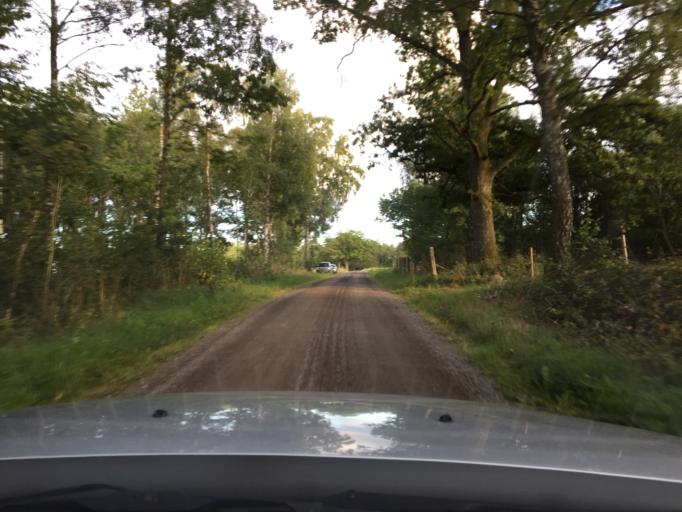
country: SE
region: Skane
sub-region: Hassleholms Kommun
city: Sosdala
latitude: 56.0342
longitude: 13.7137
